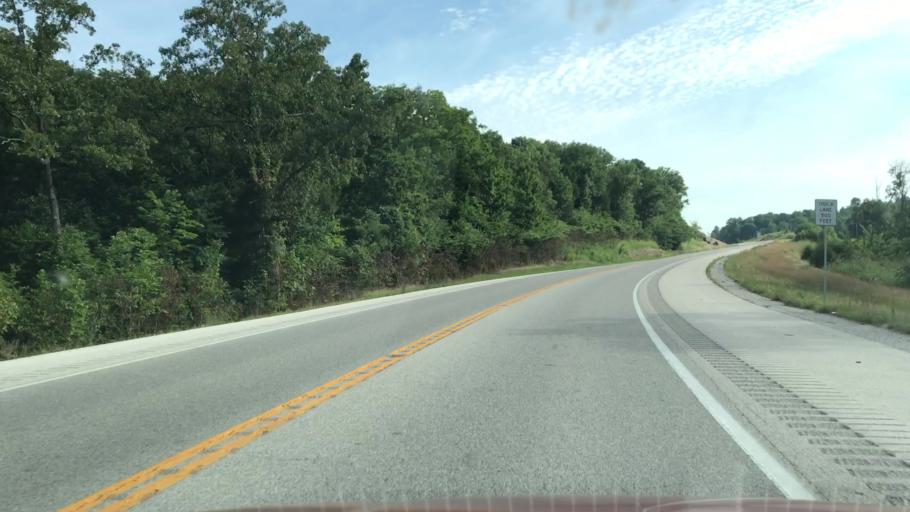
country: US
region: Kentucky
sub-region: Edmonson County
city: Brownsville
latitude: 37.0949
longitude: -86.2335
